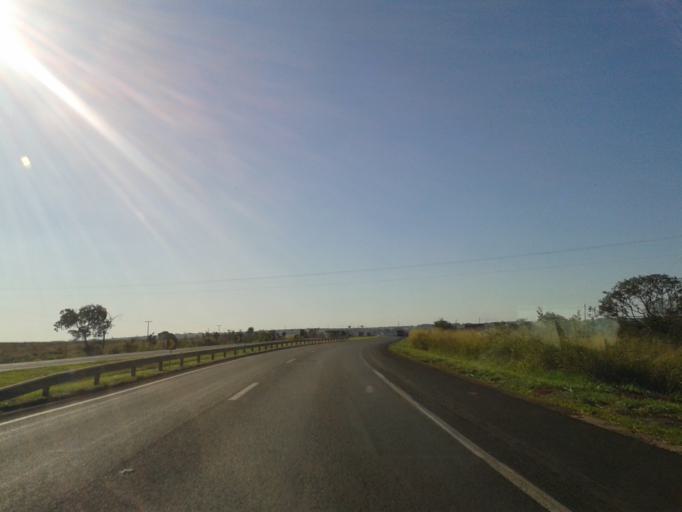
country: BR
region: Minas Gerais
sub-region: Uberlandia
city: Uberlandia
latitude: -19.0109
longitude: -48.2081
